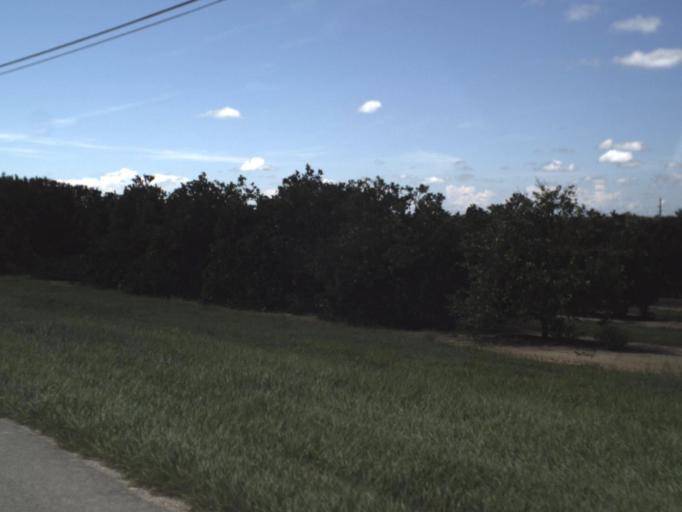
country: US
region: Florida
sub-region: Polk County
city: Lake Hamilton
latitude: 28.0624
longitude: -81.6200
